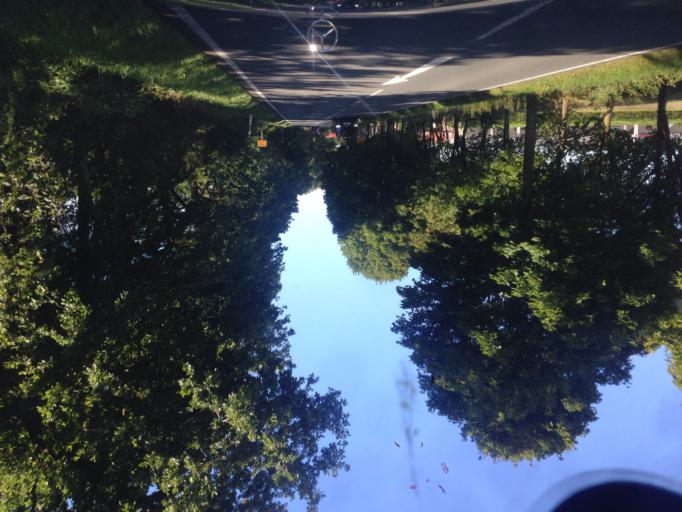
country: DE
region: Schleswig-Holstein
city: Schafflund
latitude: 54.7621
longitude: 9.1665
